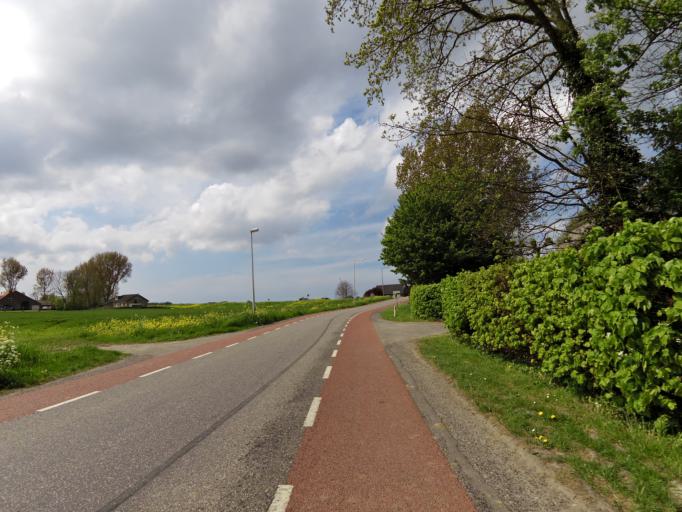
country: NL
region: South Holland
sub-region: Gemeente Spijkenisse
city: Spijkenisse
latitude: 51.8282
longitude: 4.2385
